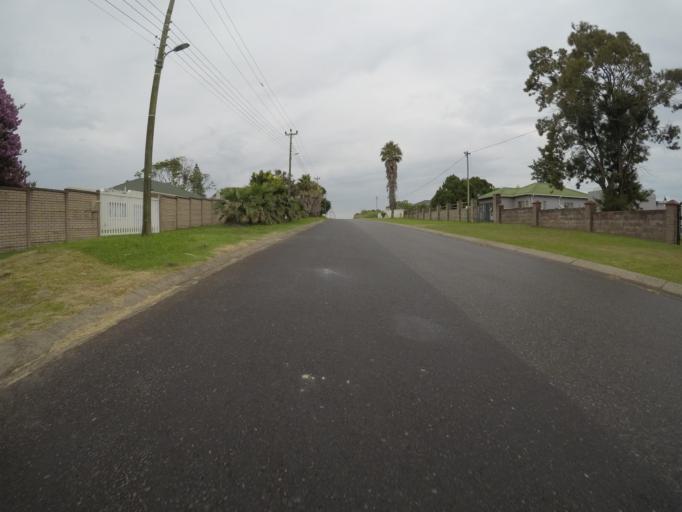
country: ZA
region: Eastern Cape
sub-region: Buffalo City Metropolitan Municipality
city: East London
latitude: -32.9645
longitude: 27.8392
